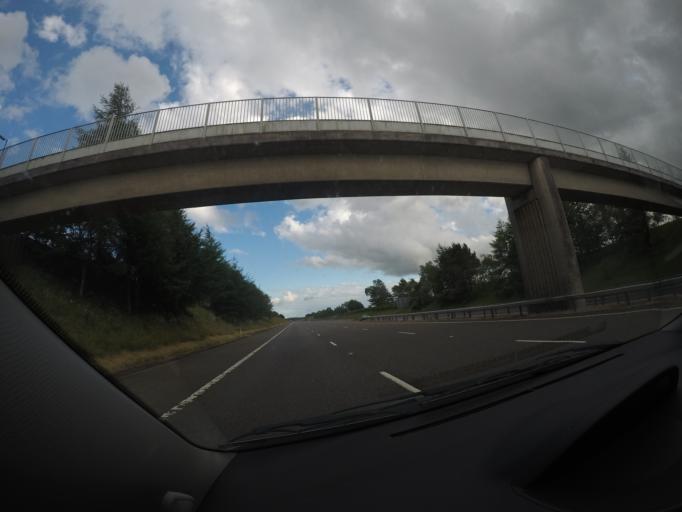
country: GB
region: Scotland
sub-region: Dumfries and Galloway
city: Lockerbie
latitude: 55.1150
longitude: -3.3591
